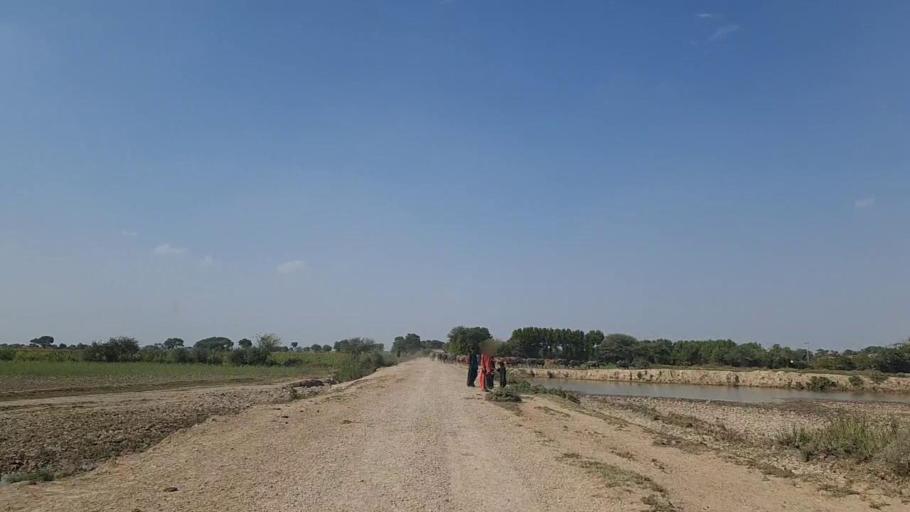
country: PK
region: Sindh
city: Jati
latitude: 24.5180
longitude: 68.2940
